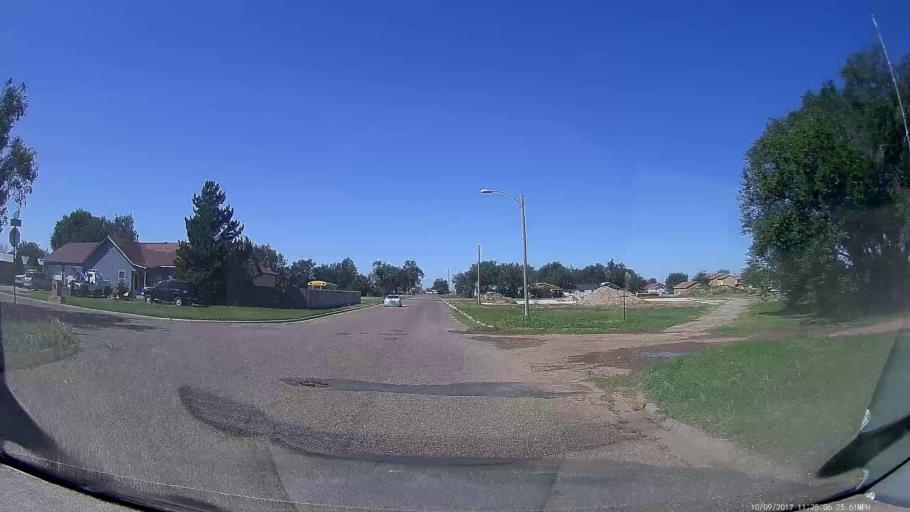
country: US
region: New Mexico
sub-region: Curry County
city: Clovis
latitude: 34.4110
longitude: -103.2196
